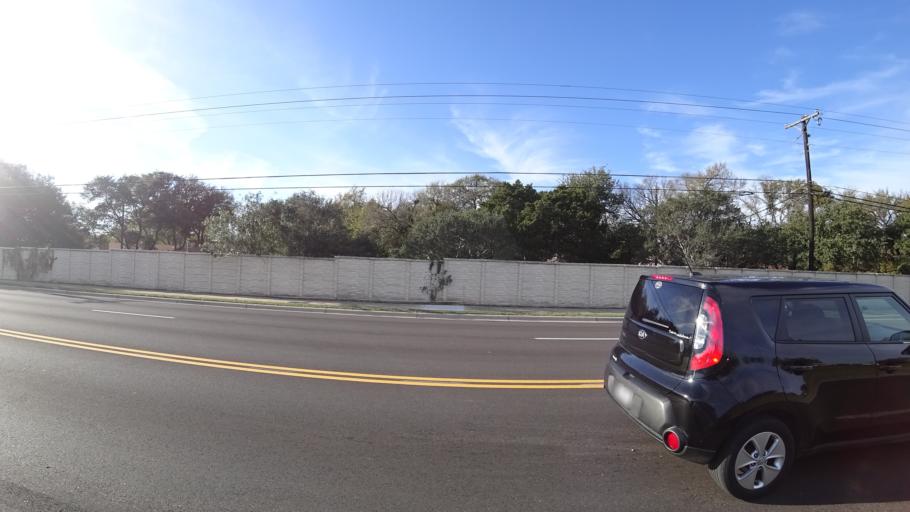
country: US
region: Texas
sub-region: Williamson County
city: Round Rock
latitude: 30.4884
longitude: -97.6979
